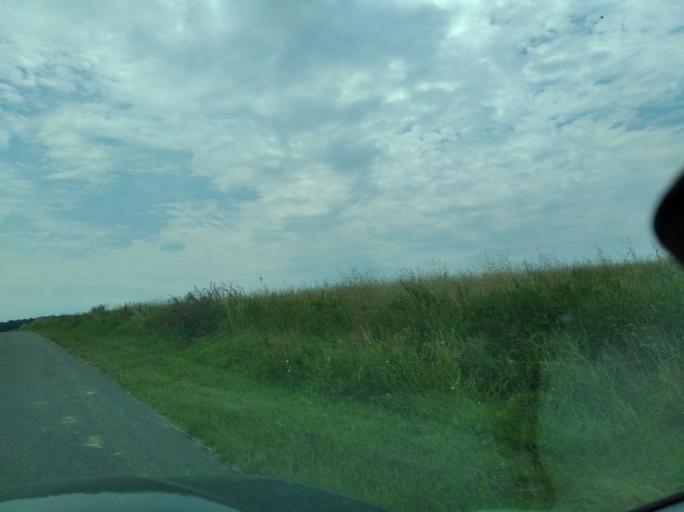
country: PL
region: Subcarpathian Voivodeship
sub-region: Powiat przeworski
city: Lopuszka Wielka
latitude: 49.9024
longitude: 22.4171
